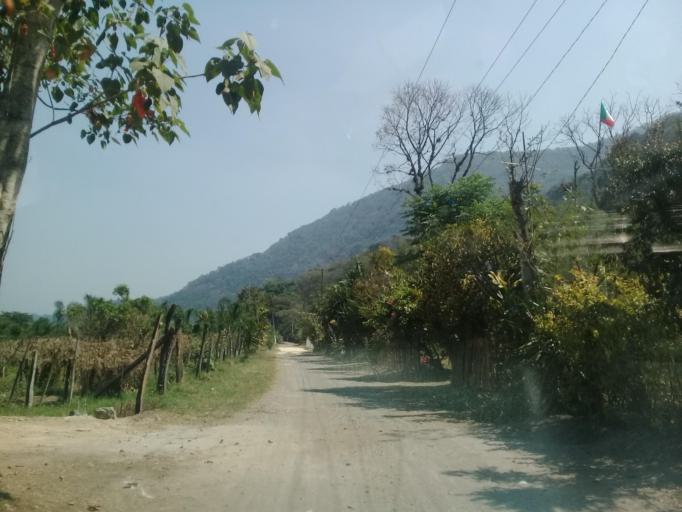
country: MX
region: Veracruz
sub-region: Ixtaczoquitlan
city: Capoluca
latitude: 18.8005
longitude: -96.9914
